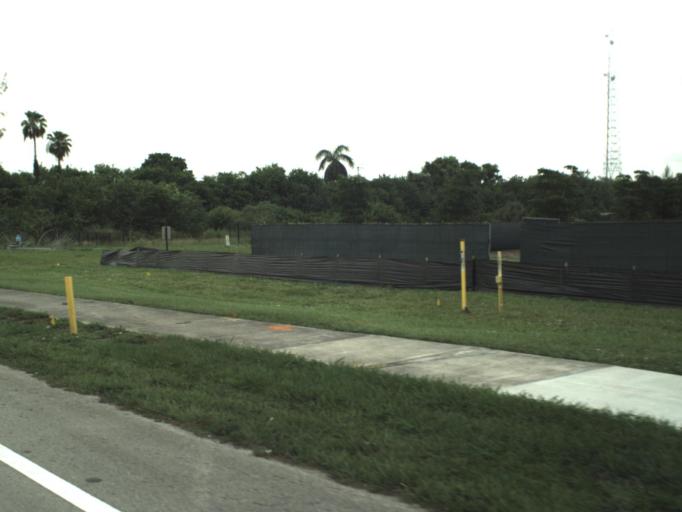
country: US
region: Florida
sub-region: Palm Beach County
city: Villages of Oriole
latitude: 26.4538
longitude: -80.1710
